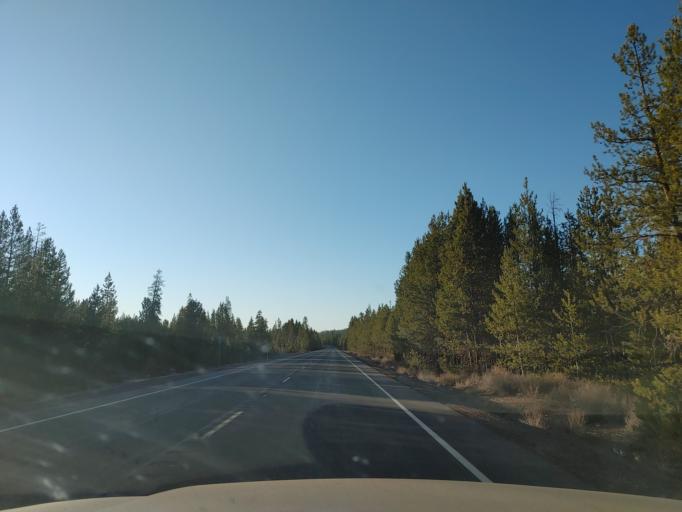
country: US
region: Oregon
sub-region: Deschutes County
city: La Pine
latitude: 43.4162
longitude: -121.8367
